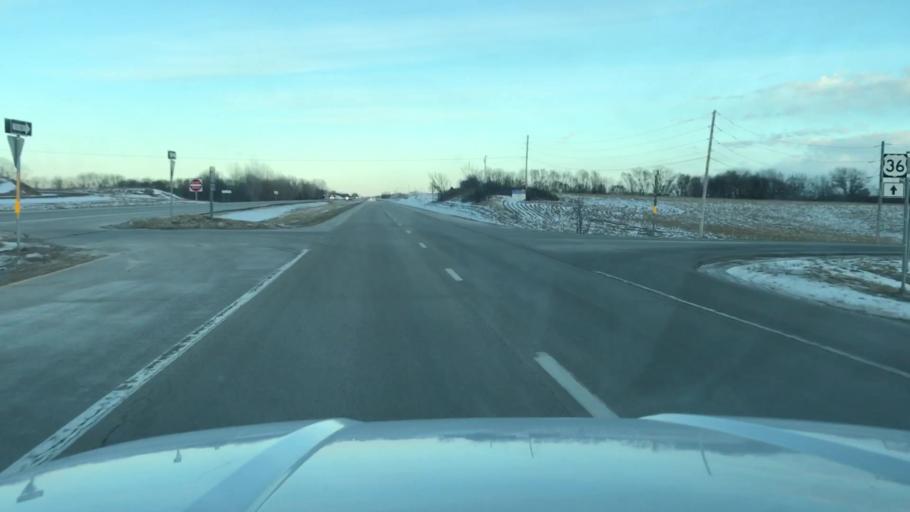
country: US
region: Missouri
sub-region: Clinton County
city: Gower
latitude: 39.7472
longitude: -94.6431
